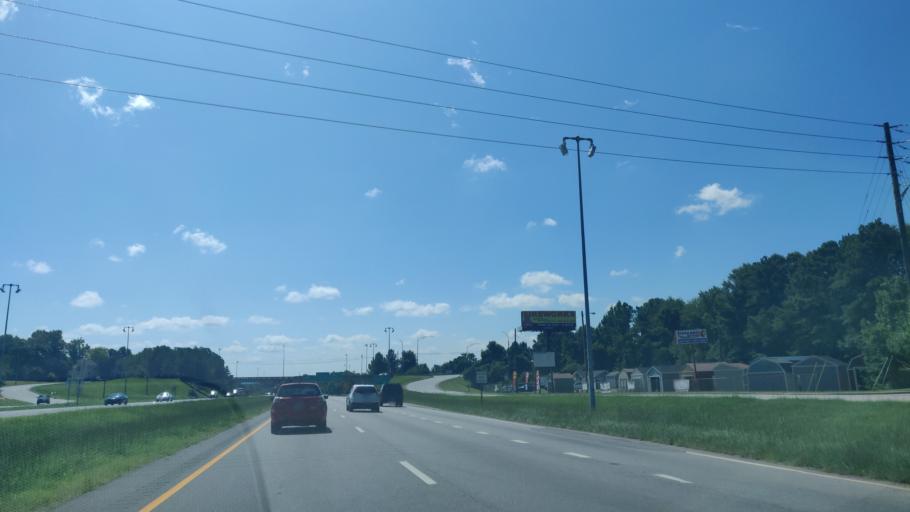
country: US
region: Alabama
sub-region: Russell County
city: Phenix City
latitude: 32.4582
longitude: -85.0148
